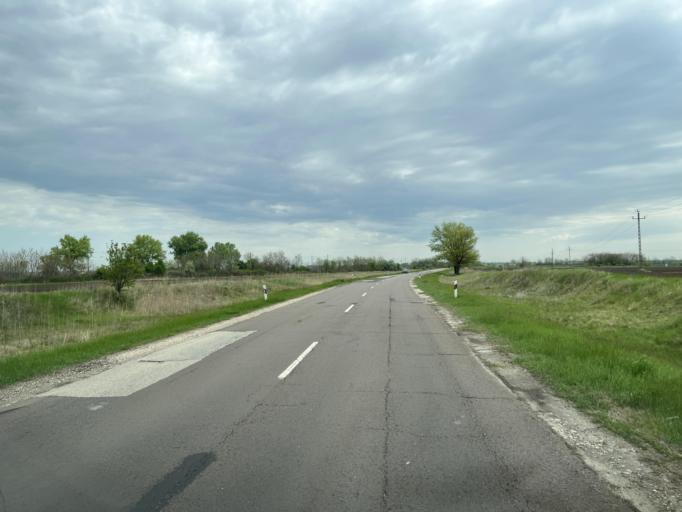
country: HU
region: Pest
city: Cegled
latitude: 47.1782
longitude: 19.8472
